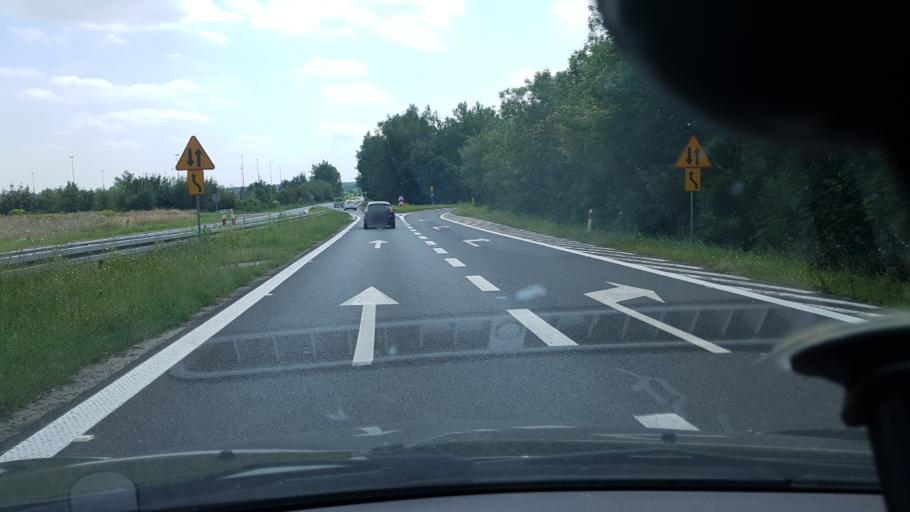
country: PL
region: Silesian Voivodeship
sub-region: Powiat bierunsko-ledzinski
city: Bierun
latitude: 50.0993
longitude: 19.0983
